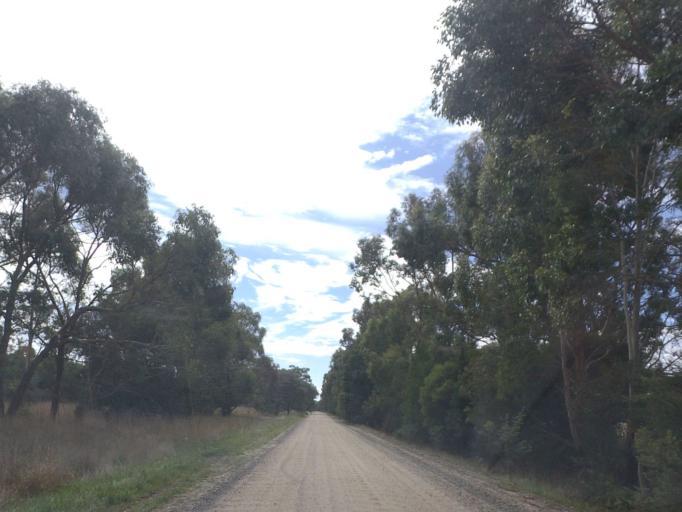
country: AU
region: Victoria
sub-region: Hume
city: Sunbury
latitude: -37.3780
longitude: 144.5507
